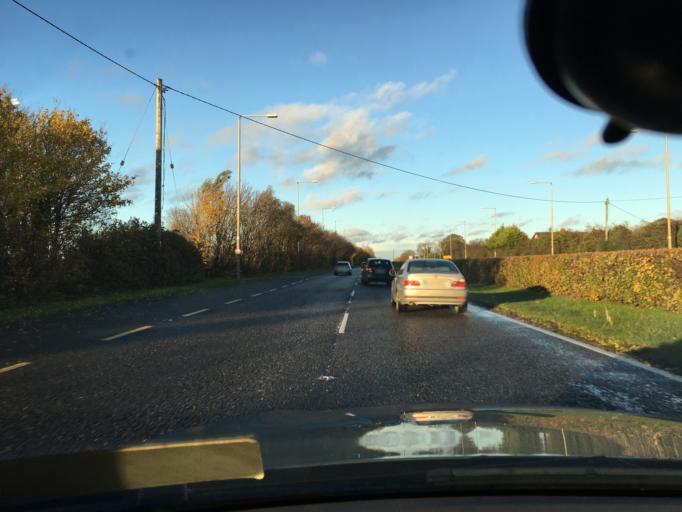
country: IE
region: Leinster
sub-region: Fingal County
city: Swords
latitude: 53.4831
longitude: -6.2015
